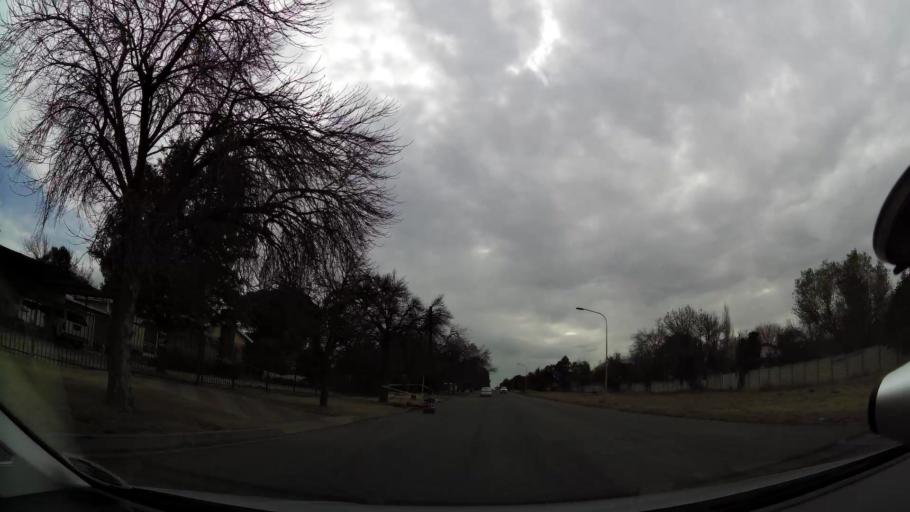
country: ZA
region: Orange Free State
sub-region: Fezile Dabi District Municipality
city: Kroonstad
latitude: -27.6390
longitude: 27.2386
